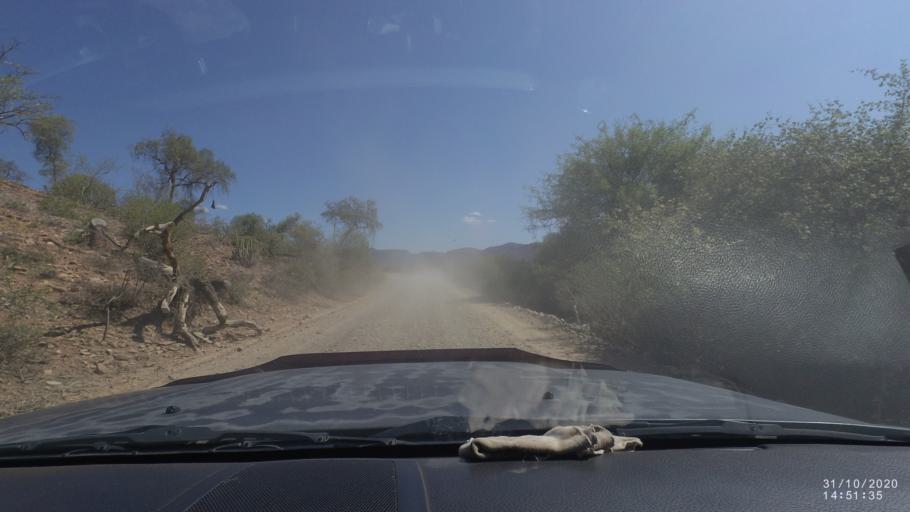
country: BO
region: Cochabamba
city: Aiquile
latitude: -18.2079
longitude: -64.8574
